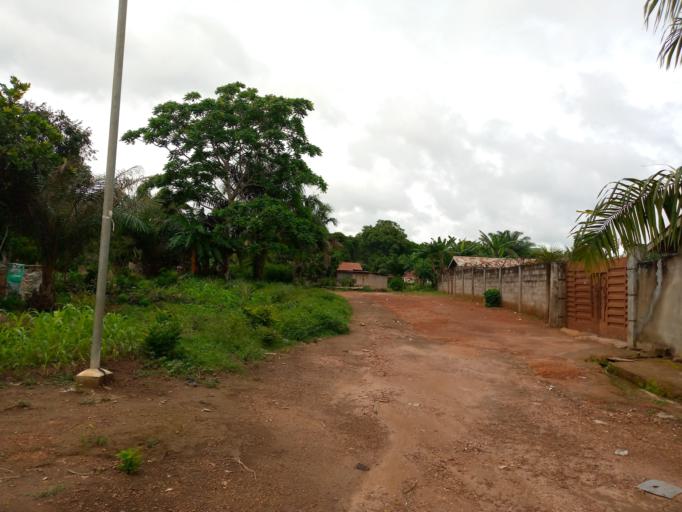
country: SL
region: Southern Province
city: Mogbwemo
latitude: 7.7656
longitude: -12.3123
